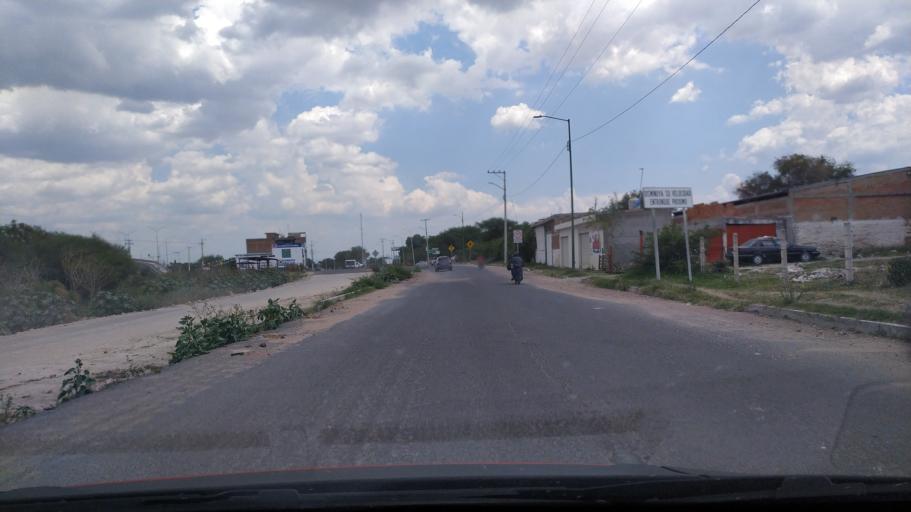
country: MX
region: Guanajuato
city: San Francisco del Rincon
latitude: 21.0458
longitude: -101.8694
